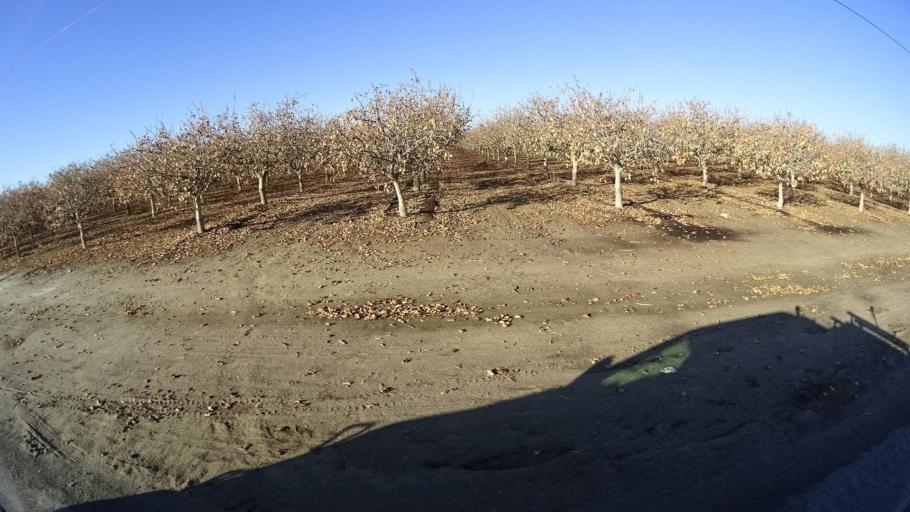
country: US
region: California
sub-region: Kern County
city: Delano
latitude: 35.7735
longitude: -119.3298
